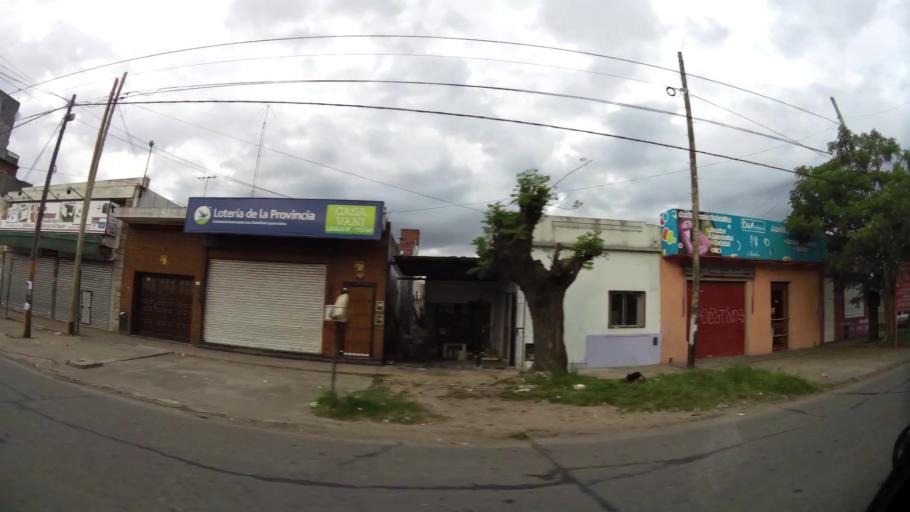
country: AR
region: Buenos Aires
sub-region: Partido de Quilmes
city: Quilmes
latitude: -34.7386
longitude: -58.2390
